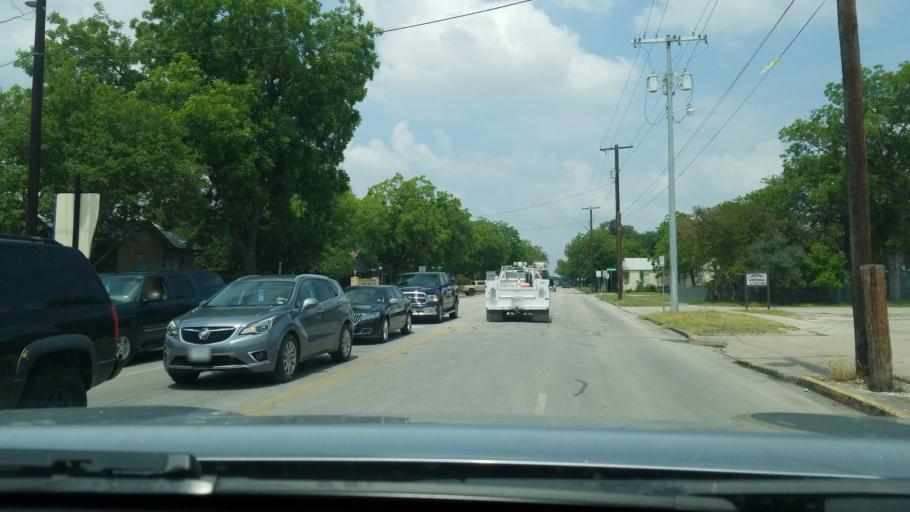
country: US
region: Texas
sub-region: Comal County
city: New Braunfels
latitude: 29.7100
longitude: -98.1196
